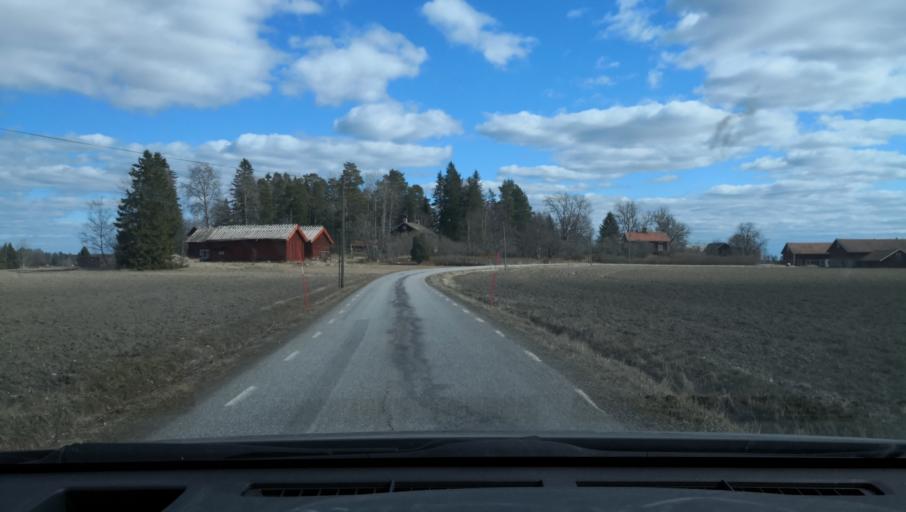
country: SE
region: Vaestmanland
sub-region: Sala Kommun
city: Sala
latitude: 59.8641
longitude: 16.5690
